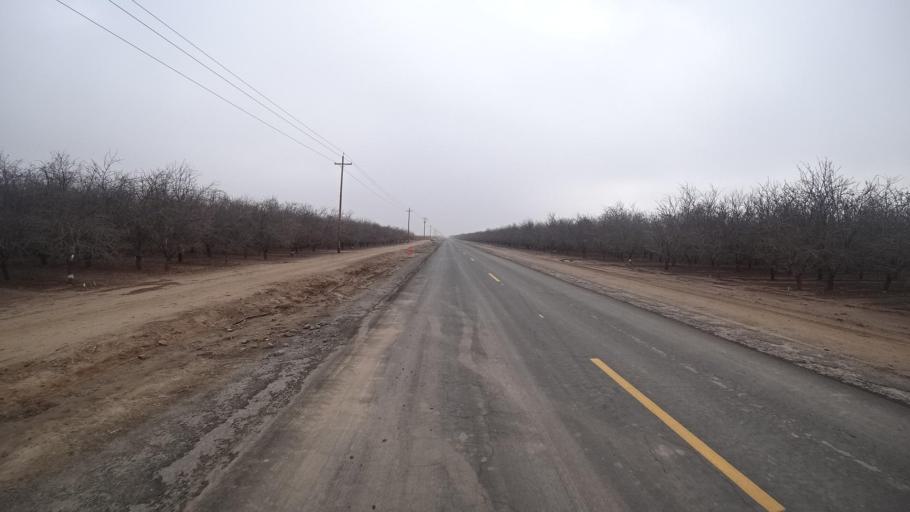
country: US
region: California
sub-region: Kern County
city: Maricopa
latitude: 35.0938
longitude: -119.2542
